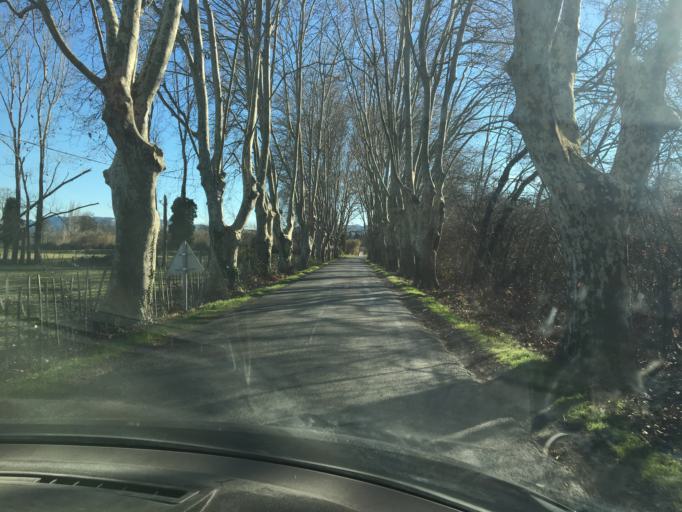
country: FR
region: Provence-Alpes-Cote d'Azur
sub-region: Departement des Bouches-du-Rhone
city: Maillane
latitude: 43.8058
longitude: 4.7861
